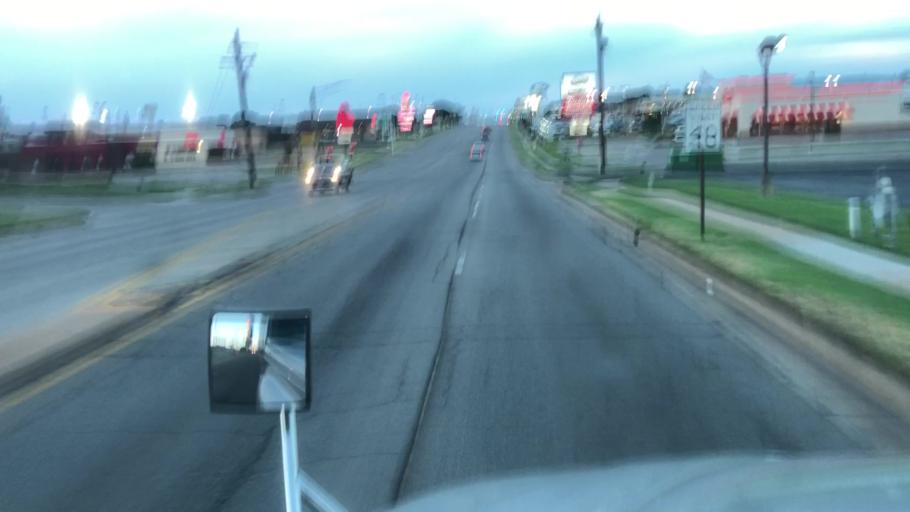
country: US
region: Oklahoma
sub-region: Kay County
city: Ponca City
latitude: 36.7318
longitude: -97.0672
